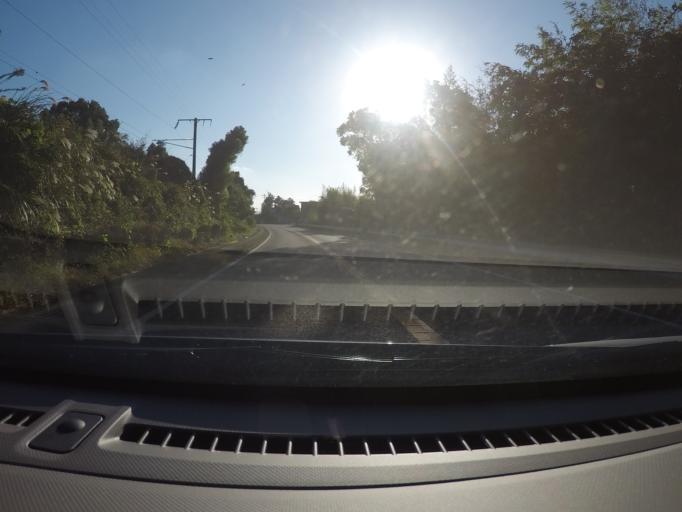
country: JP
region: Kagoshima
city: Izumi
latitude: 32.1459
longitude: 130.3575
